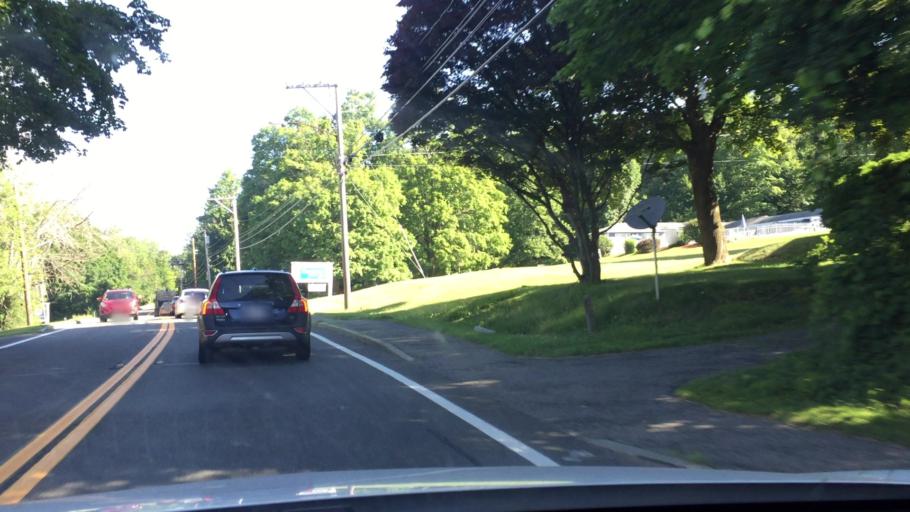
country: US
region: Massachusetts
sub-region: Berkshire County
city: Lee
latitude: 42.3153
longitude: -73.2562
